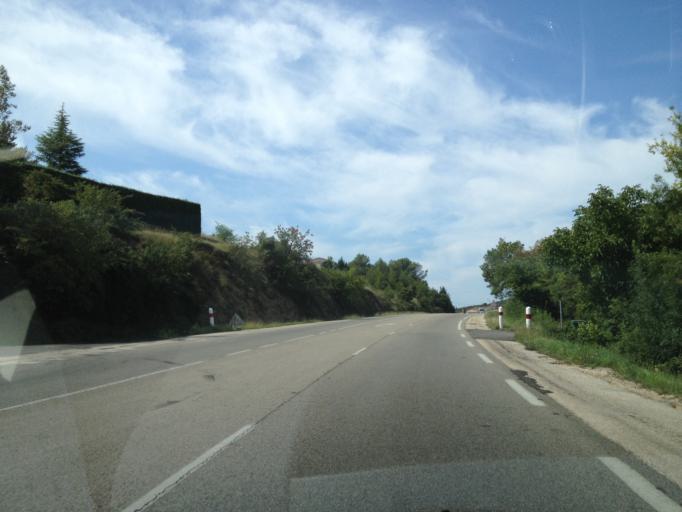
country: FR
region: Languedoc-Roussillon
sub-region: Departement du Gard
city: Rousson
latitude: 44.2116
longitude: 4.1471
